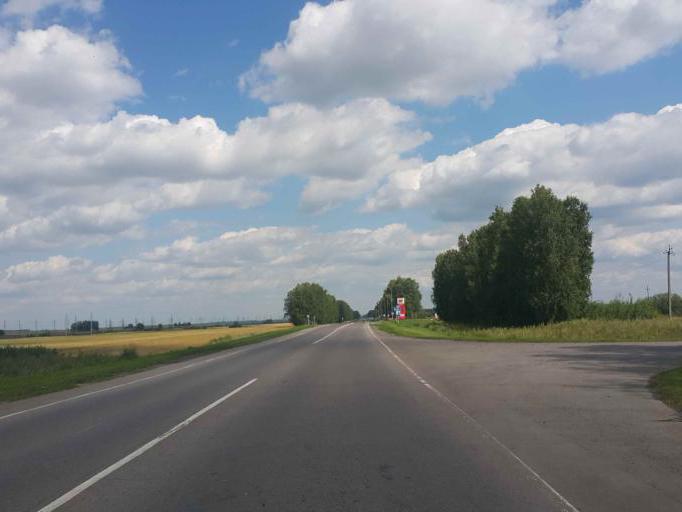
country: RU
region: Tambov
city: Goreloye
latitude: 53.0407
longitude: 41.4676
